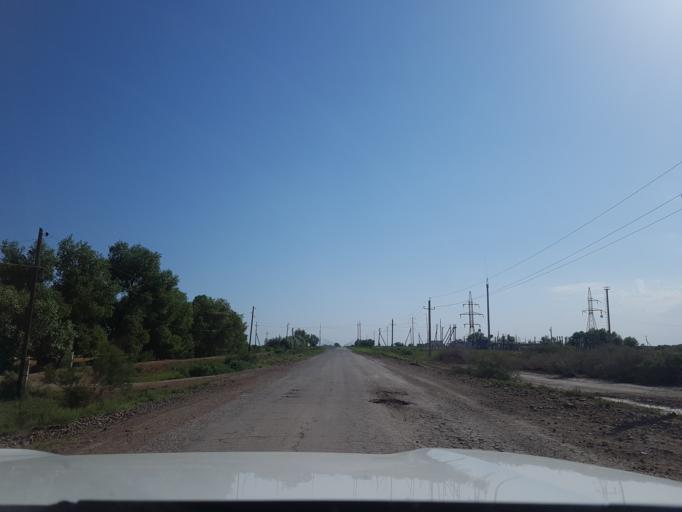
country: TM
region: Dasoguz
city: Koeneuergench
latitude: 42.0973
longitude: 58.8978
